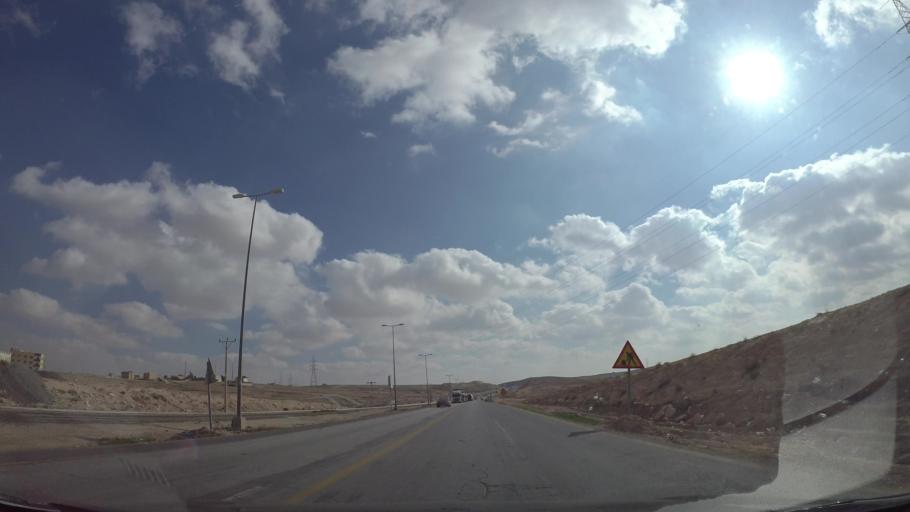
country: JO
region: Amman
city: Al Jizah
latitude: 31.6050
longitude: 35.9988
